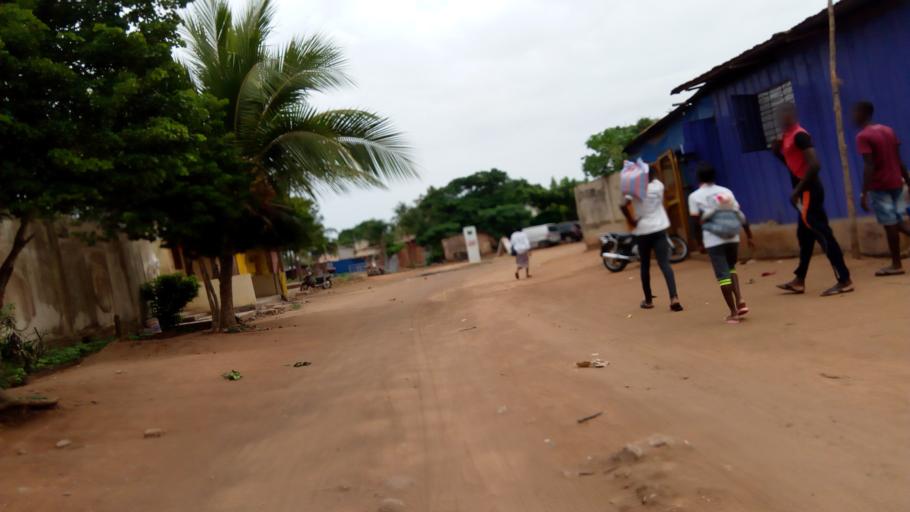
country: TG
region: Maritime
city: Lome
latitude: 6.1802
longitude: 1.1864
